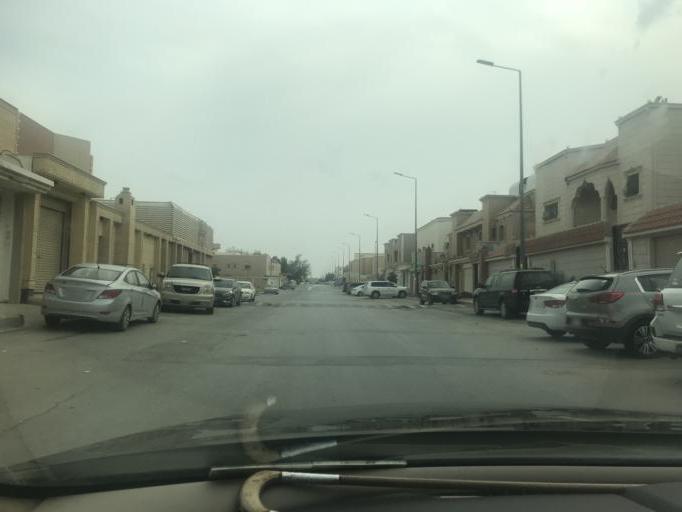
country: SA
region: Ar Riyad
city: Riyadh
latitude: 24.7496
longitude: 46.7689
